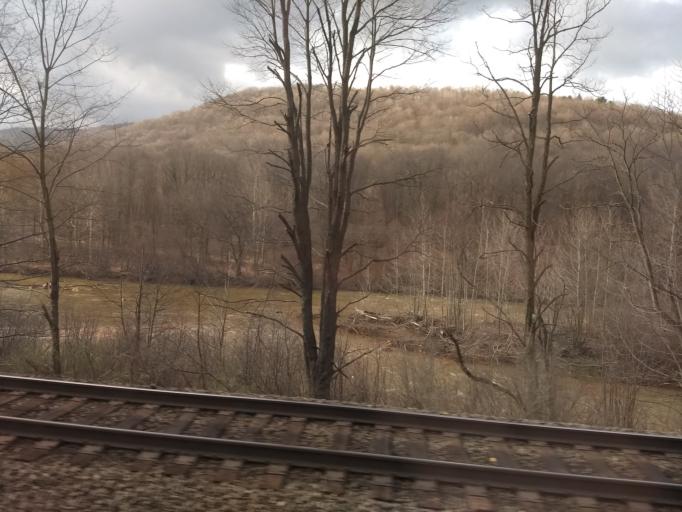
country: US
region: Pennsylvania
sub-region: Cambria County
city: Vinco
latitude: 40.3700
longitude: -78.8084
